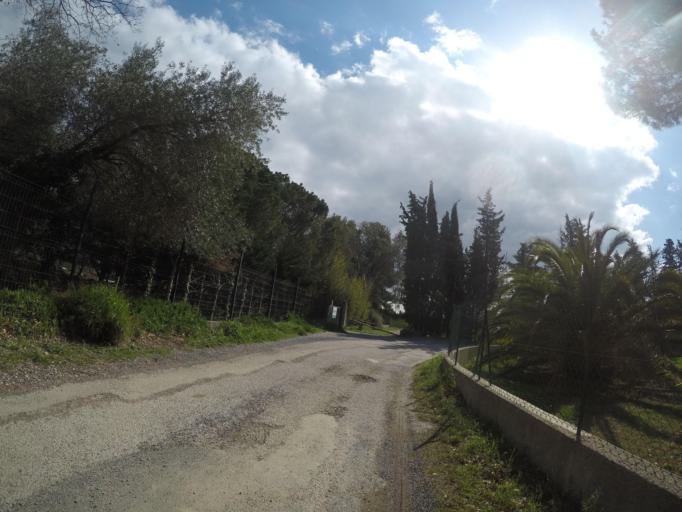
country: FR
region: Languedoc-Roussillon
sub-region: Departement des Pyrenees-Orientales
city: Pezilla-la-Riviere
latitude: 42.6702
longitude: 2.7683
